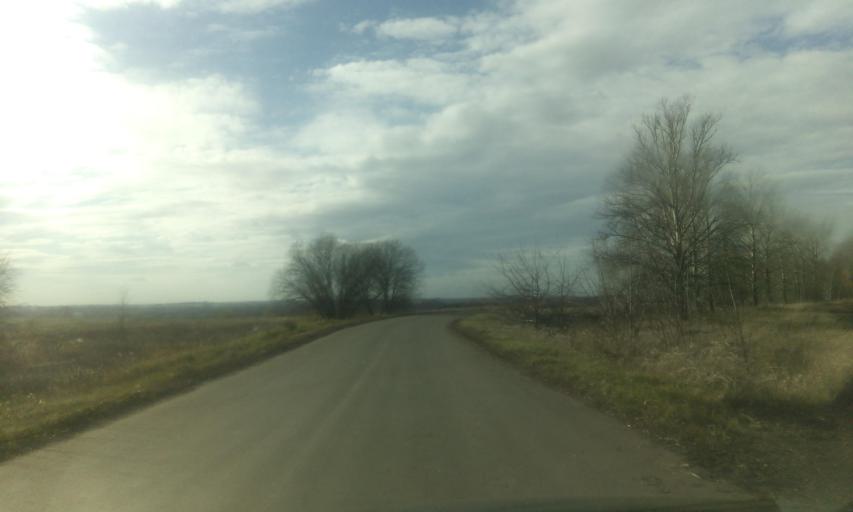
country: RU
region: Tula
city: Dubovka
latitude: 53.9583
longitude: 38.0531
